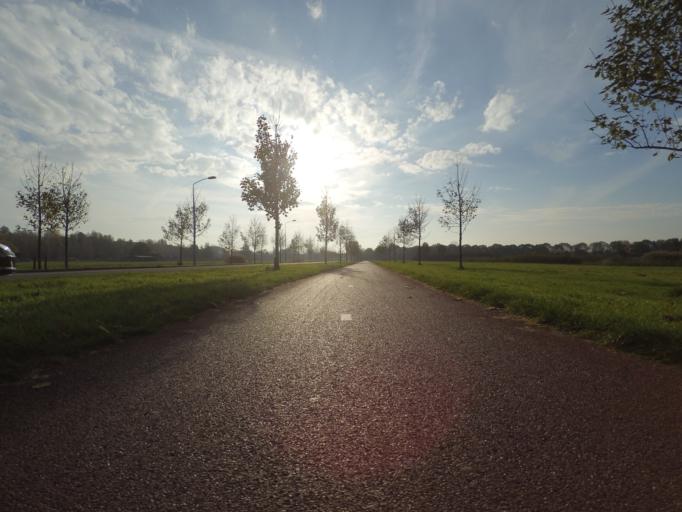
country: NL
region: Flevoland
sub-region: Gemeente Zeewolde
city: Zeewolde
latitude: 52.3398
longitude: 5.5315
